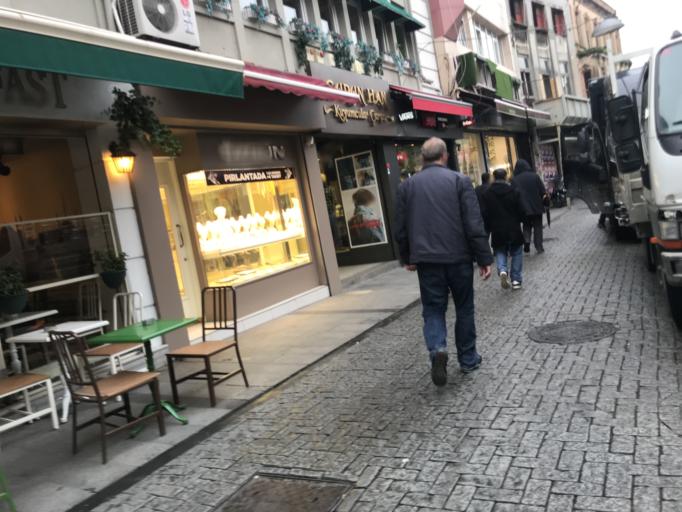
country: TR
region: Istanbul
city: Sisli
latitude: 41.0435
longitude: 29.0057
